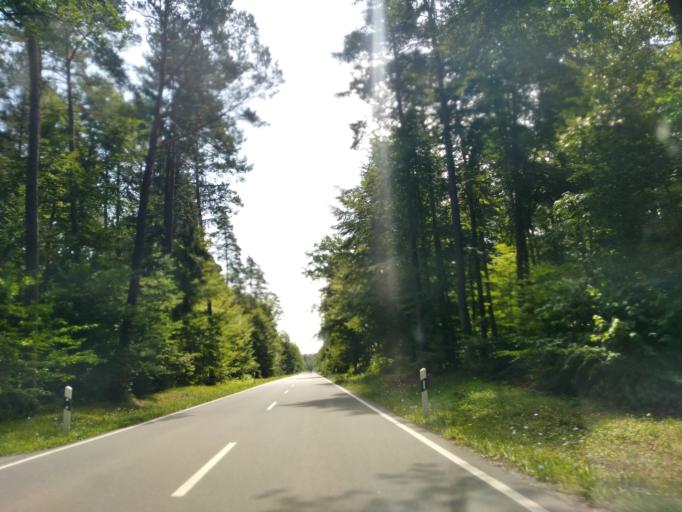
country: DE
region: Baden-Wuerttemberg
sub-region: Karlsruhe Region
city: Limbach
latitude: 49.5013
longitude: 9.2425
